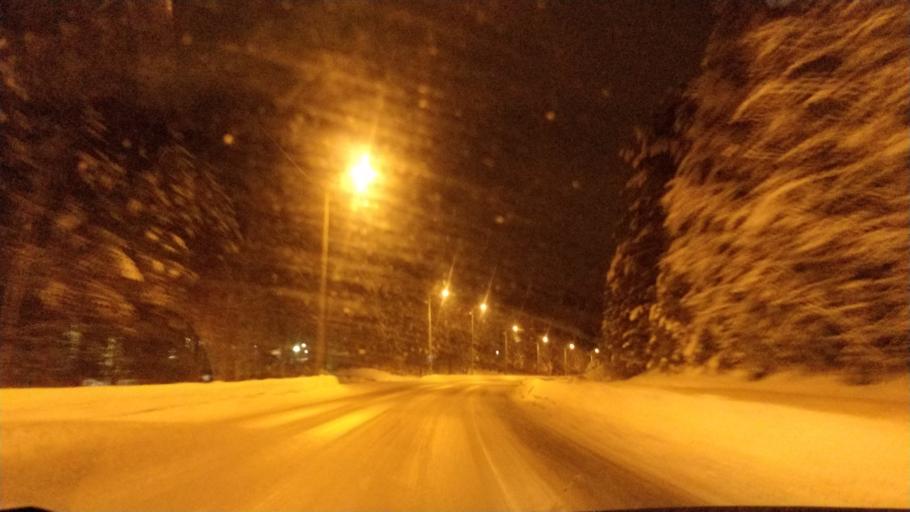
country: FI
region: Lapland
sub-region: Rovaniemi
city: Rovaniemi
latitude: 66.3769
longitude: 25.3828
